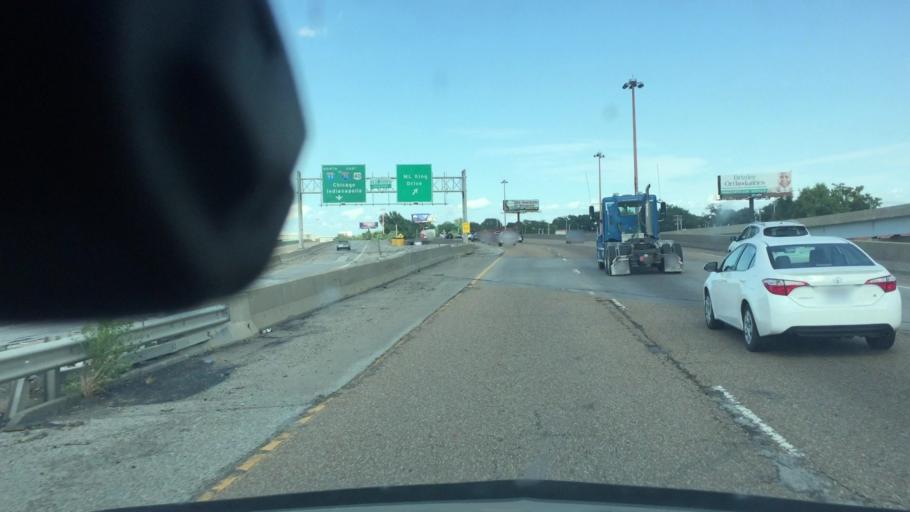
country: US
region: Illinois
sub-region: Saint Clair County
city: East Saint Louis
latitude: 38.6286
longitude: -90.1596
